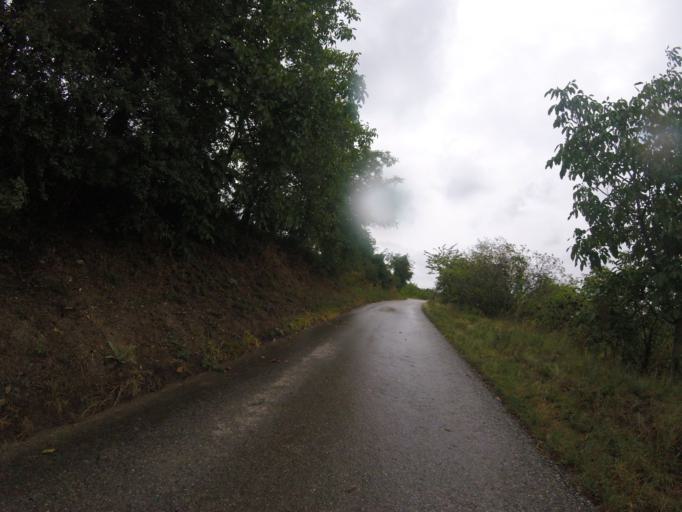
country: AT
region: Burgenland
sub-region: Eisenstadt-Umgebung
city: Donnerskirchen
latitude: 47.9117
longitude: 16.6614
